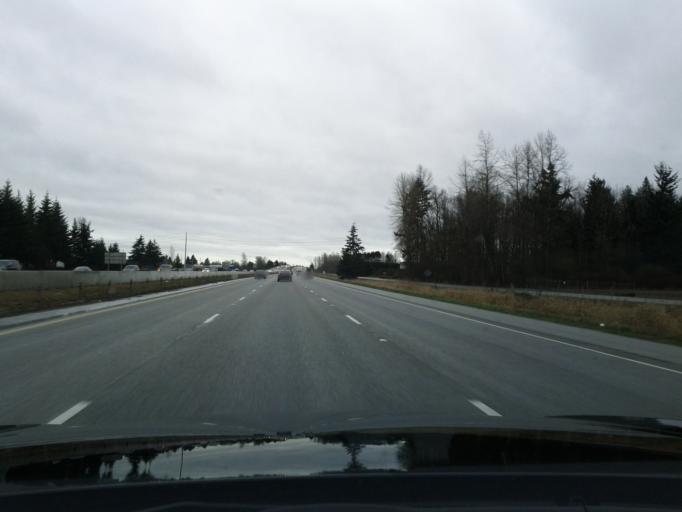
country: US
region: Washington
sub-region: Snohomish County
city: Smokey Point
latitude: 48.1356
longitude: -122.1864
